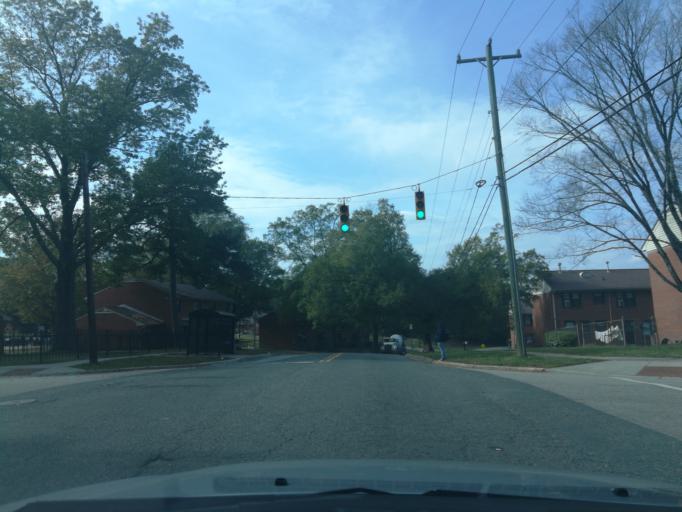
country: US
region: North Carolina
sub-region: Durham County
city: Durham
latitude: 35.9739
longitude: -78.8876
